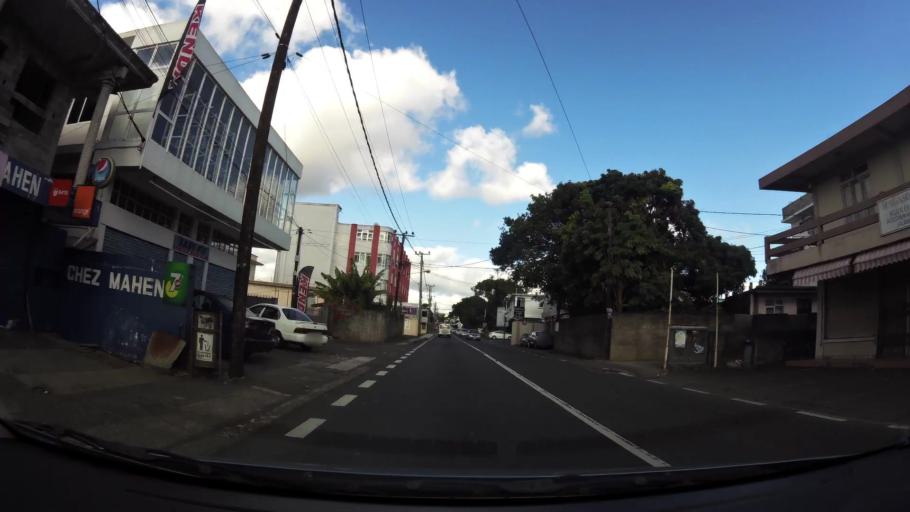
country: MU
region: Plaines Wilhems
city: Vacoas
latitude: -20.2818
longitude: 57.5029
